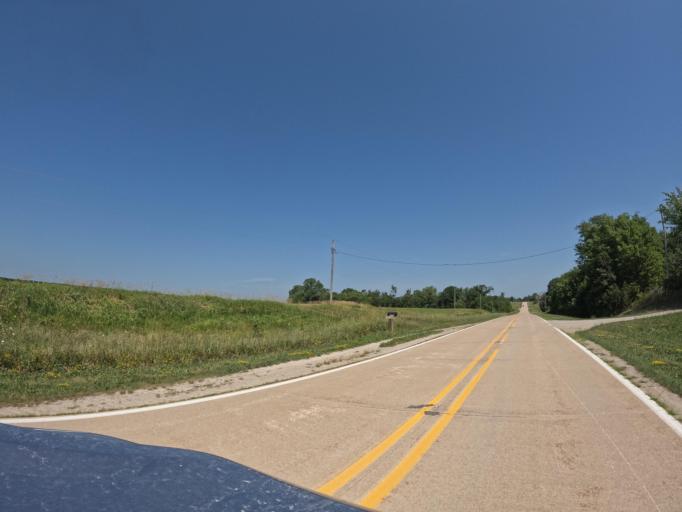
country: US
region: Iowa
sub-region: Henry County
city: Mount Pleasant
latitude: 40.8798
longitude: -91.5602
